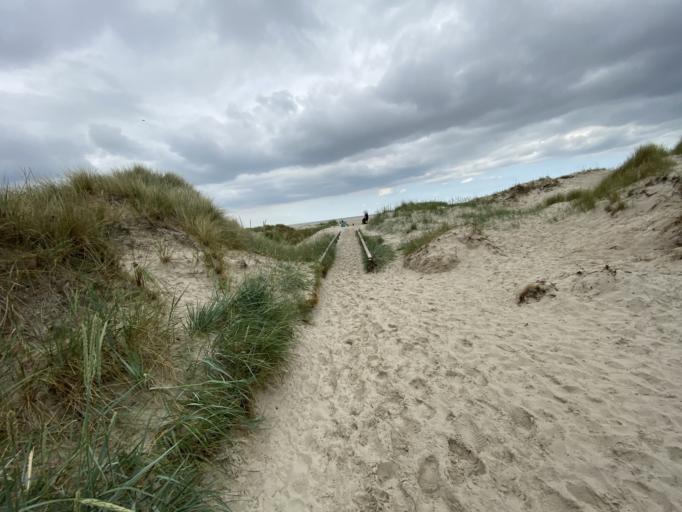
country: DE
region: Schleswig-Holstein
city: Sankt Peter-Ording
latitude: 54.3420
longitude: 8.6049
